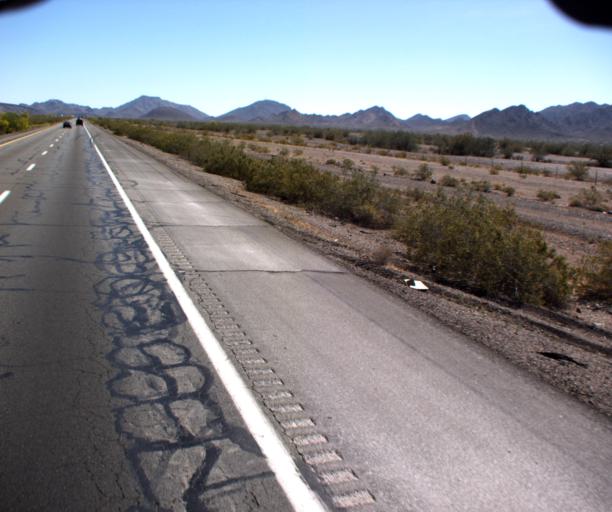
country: US
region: Arizona
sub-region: La Paz County
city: Quartzsite
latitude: 33.6734
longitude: -114.1397
